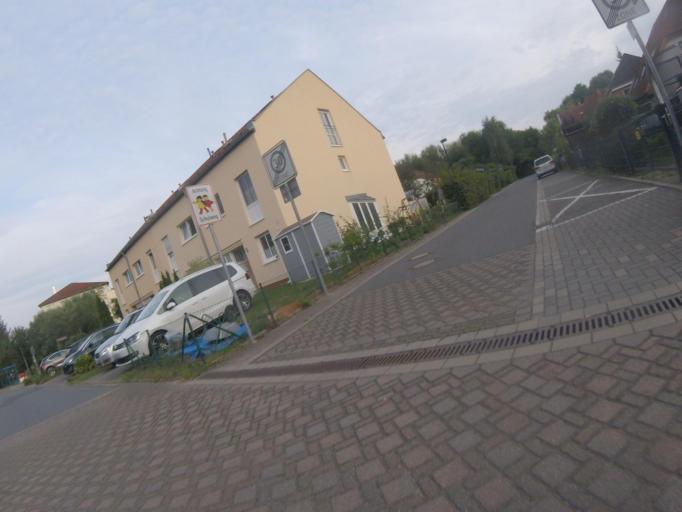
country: DE
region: Brandenburg
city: Wildau
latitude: 52.3288
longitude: 13.6220
